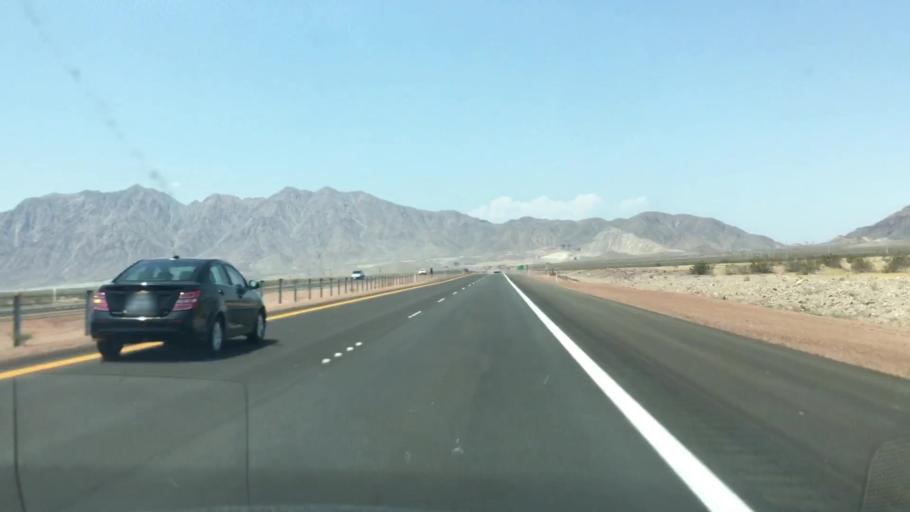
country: US
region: Nevada
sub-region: Clark County
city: Boulder City
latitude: 35.9395
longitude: -114.8740
